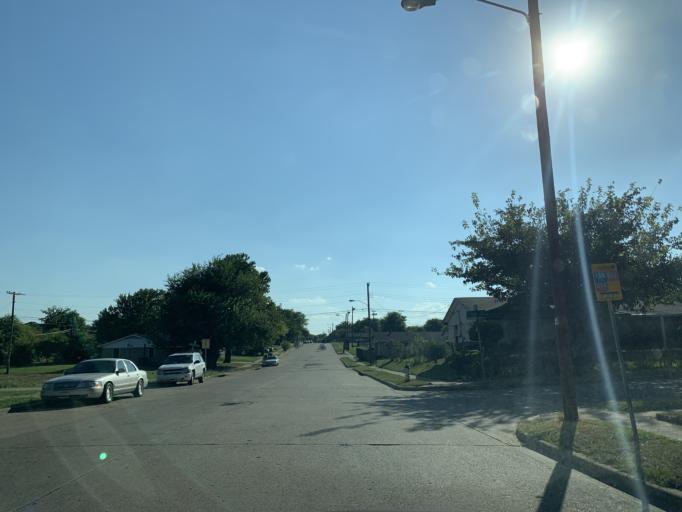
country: US
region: Texas
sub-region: Dallas County
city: Hutchins
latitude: 32.6607
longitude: -96.7632
